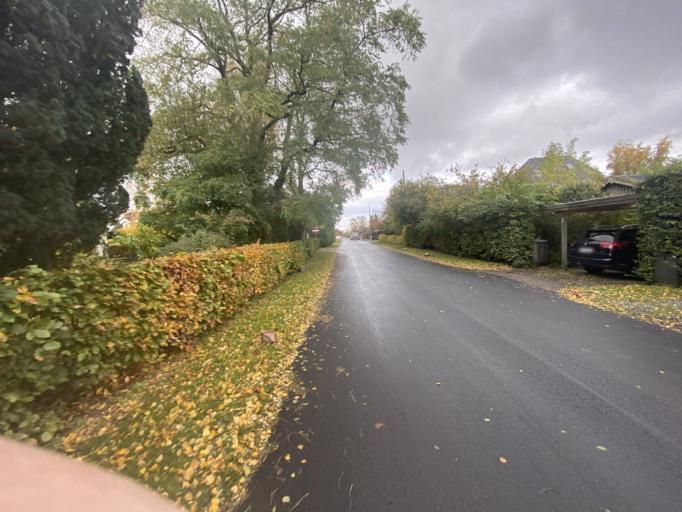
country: DK
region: Capital Region
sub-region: Dragor Kommune
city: Dragor
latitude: 55.6020
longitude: 12.6675
